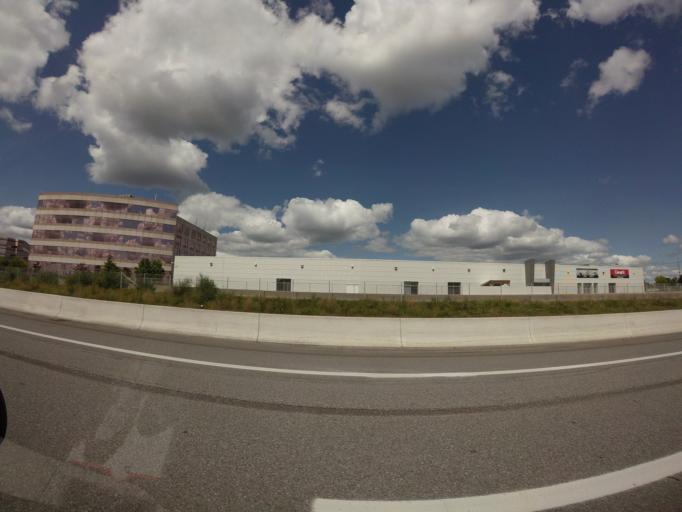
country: CA
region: Ontario
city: Ottawa
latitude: 45.4214
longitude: -75.6285
